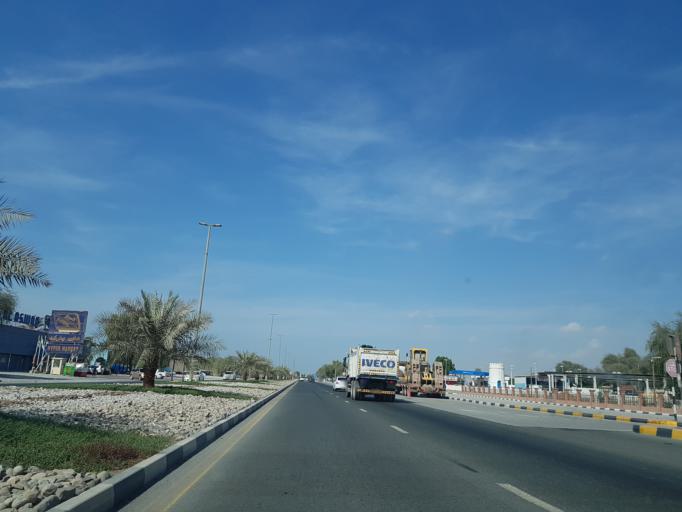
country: AE
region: Ra's al Khaymah
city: Ras al-Khaimah
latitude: 25.7058
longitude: 55.9697
